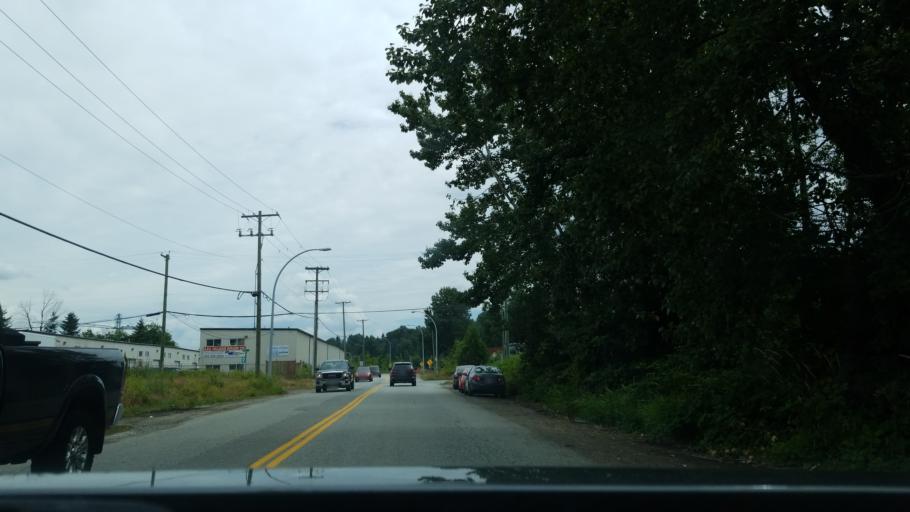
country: CA
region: British Columbia
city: New Westminster
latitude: 49.2113
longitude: -122.8561
